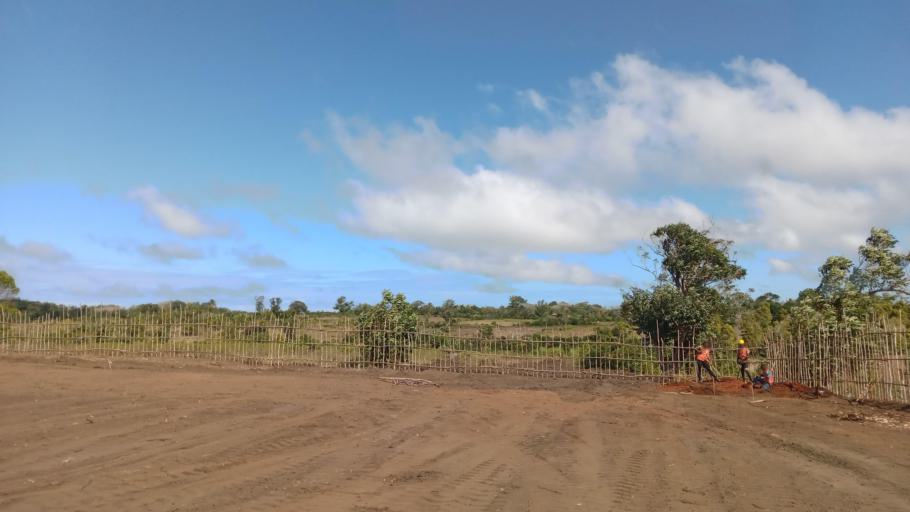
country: MG
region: Atsimo-Atsinanana
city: Vohipaho
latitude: -23.8329
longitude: 47.5531
